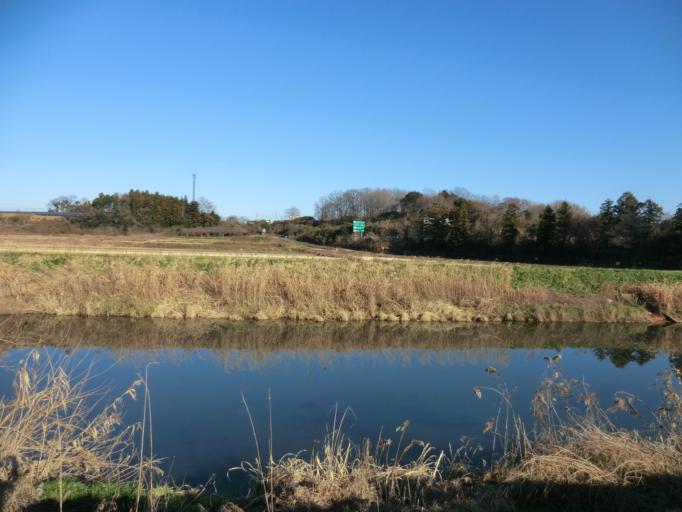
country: JP
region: Ibaraki
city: Ushiku
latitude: 36.0278
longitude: 140.0830
